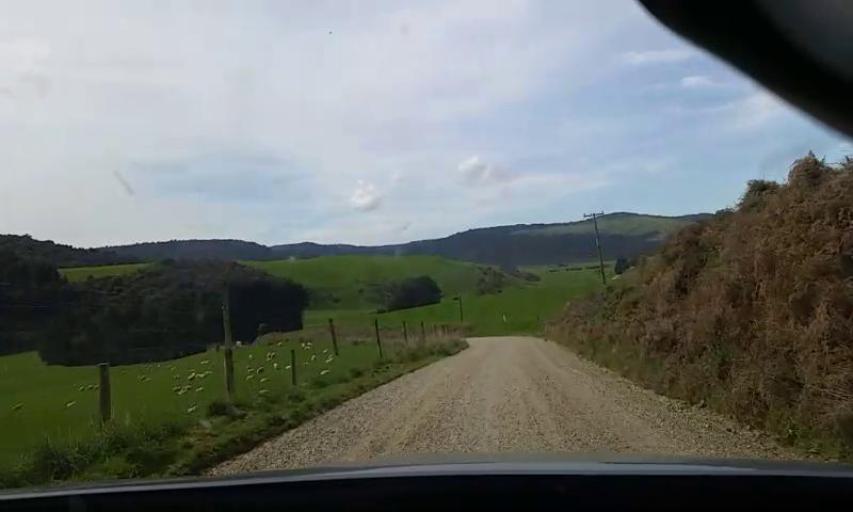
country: NZ
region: Otago
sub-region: Clutha District
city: Papatowai
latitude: -46.6272
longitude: 168.9921
